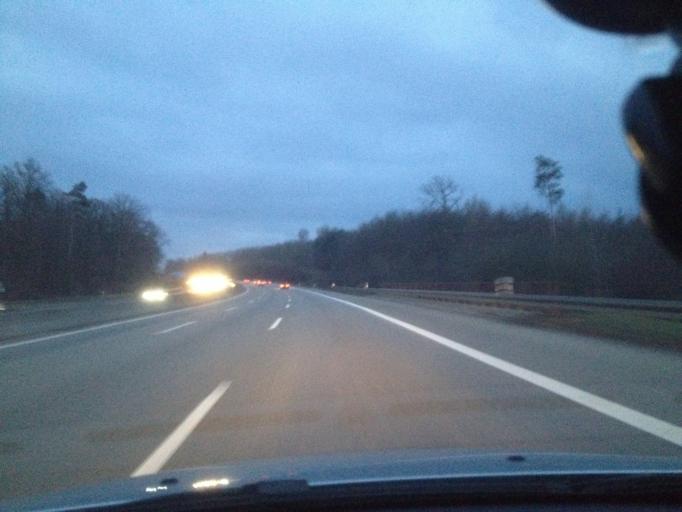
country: DE
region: Baden-Wuerttemberg
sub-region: Karlsruhe Region
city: Ispringen
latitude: 48.9104
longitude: 8.6268
